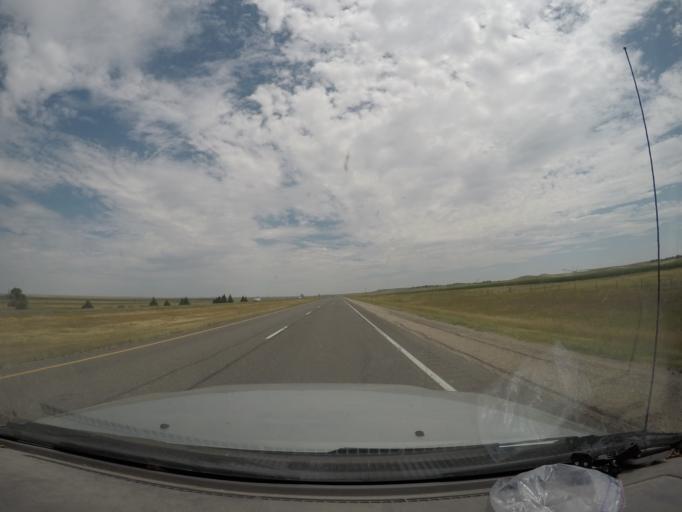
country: US
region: Wyoming
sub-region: Laramie County
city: Pine Bluffs
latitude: 41.1863
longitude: -104.0261
